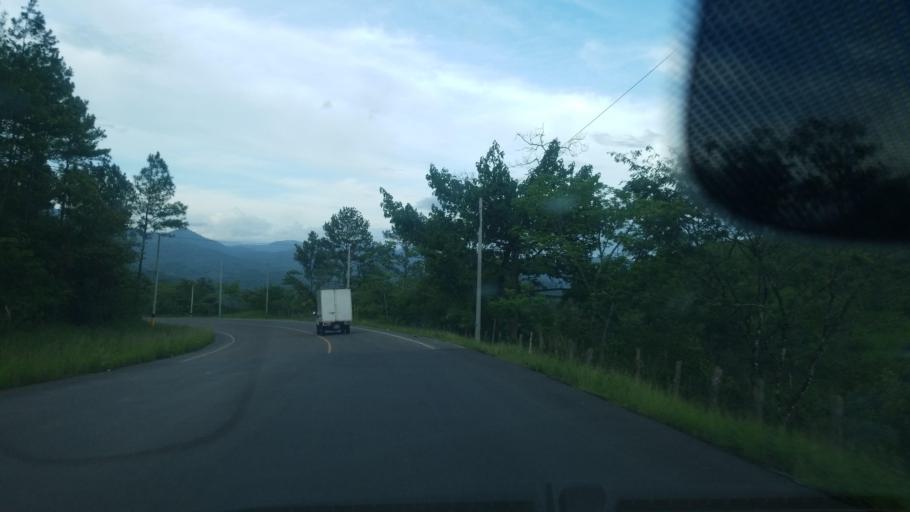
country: HN
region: Santa Barbara
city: Concepcion del Sur
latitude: 14.7962
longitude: -88.1582
